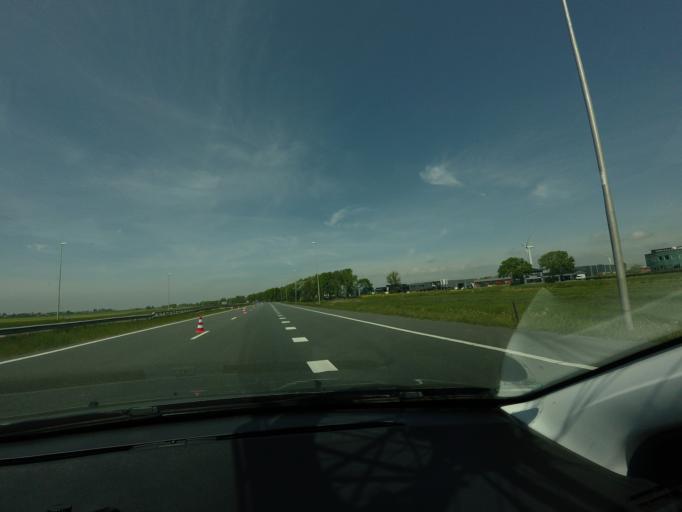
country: NL
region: Friesland
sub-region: Sudwest Fryslan
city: Bolsward
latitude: 53.0649
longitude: 5.4985
